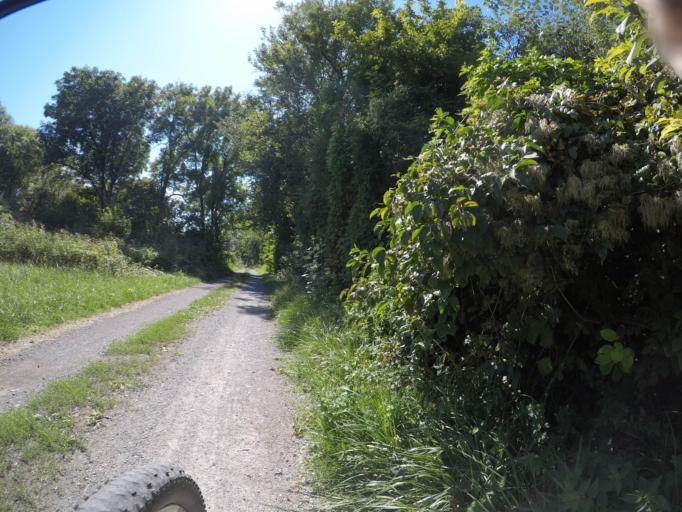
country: AT
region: Lower Austria
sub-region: Politischer Bezirk Wien-Umgebung
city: Moosbrunn
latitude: 48.0096
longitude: 16.4454
